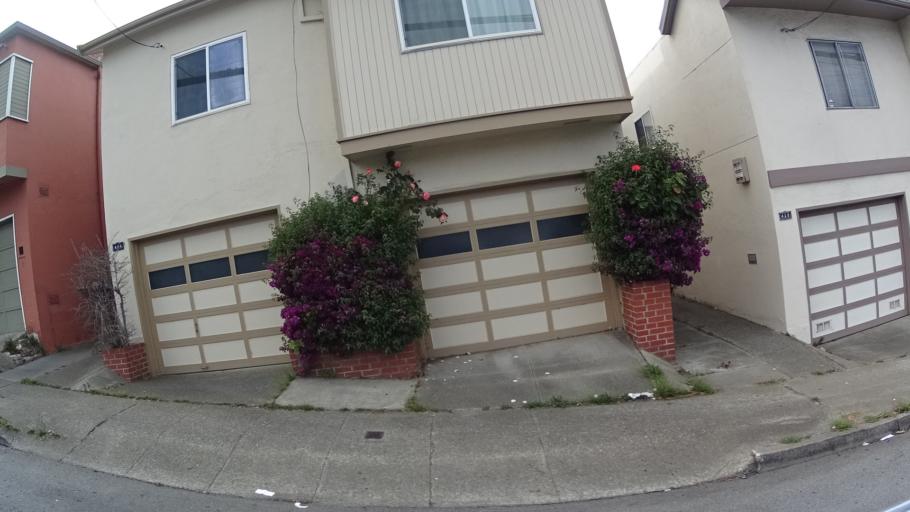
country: US
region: California
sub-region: San Mateo County
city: Daly City
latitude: 37.7095
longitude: -122.4397
